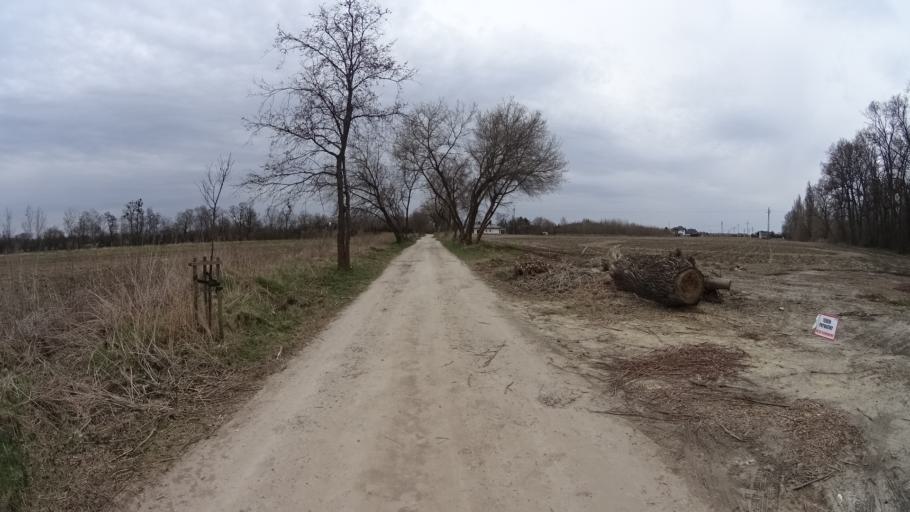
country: PL
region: Masovian Voivodeship
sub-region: Powiat warszawski zachodni
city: Ozarow Mazowiecki
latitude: 52.2340
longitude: 20.7877
